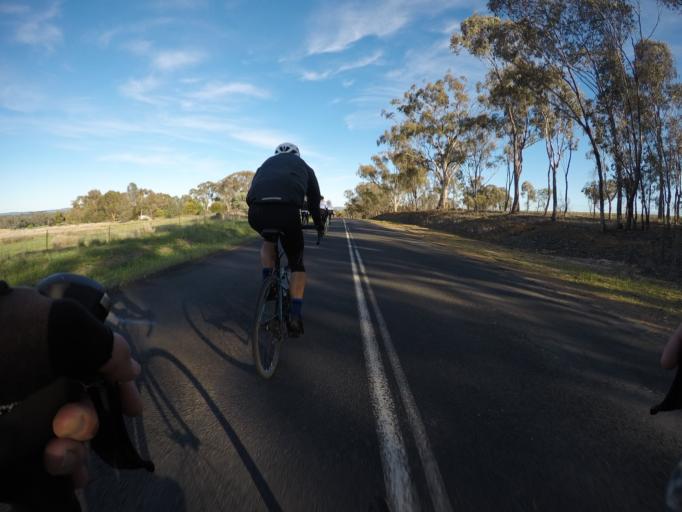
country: AU
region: New South Wales
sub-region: Cabonne
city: Molong
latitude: -32.9617
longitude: 148.7692
